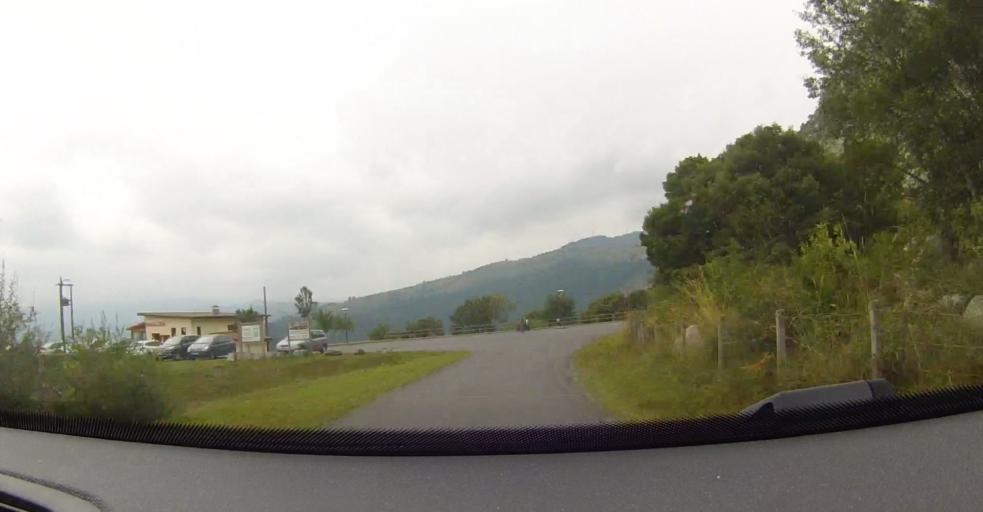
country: ES
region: Cantabria
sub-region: Provincia de Cantabria
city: Rasines
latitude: 43.2603
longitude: -3.3840
